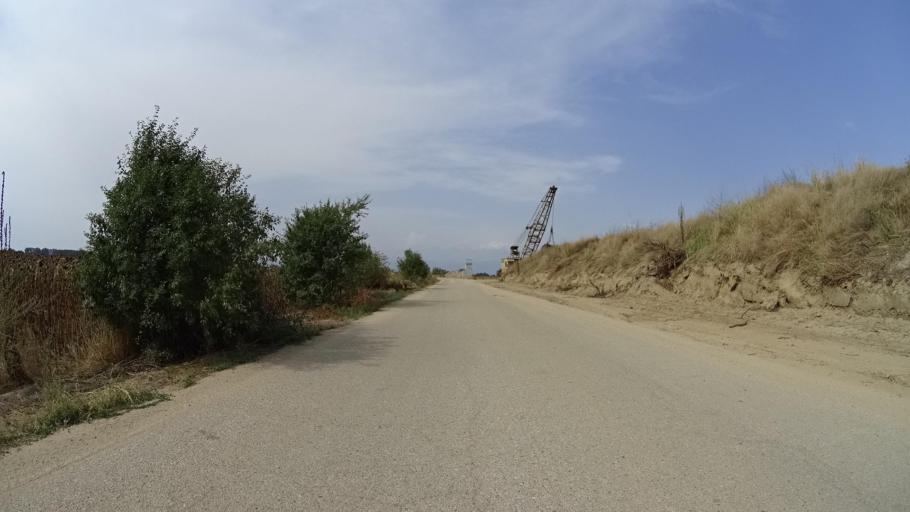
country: BG
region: Plovdiv
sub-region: Obshtina Kaloyanovo
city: Kaloyanovo
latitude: 42.3115
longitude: 24.7997
